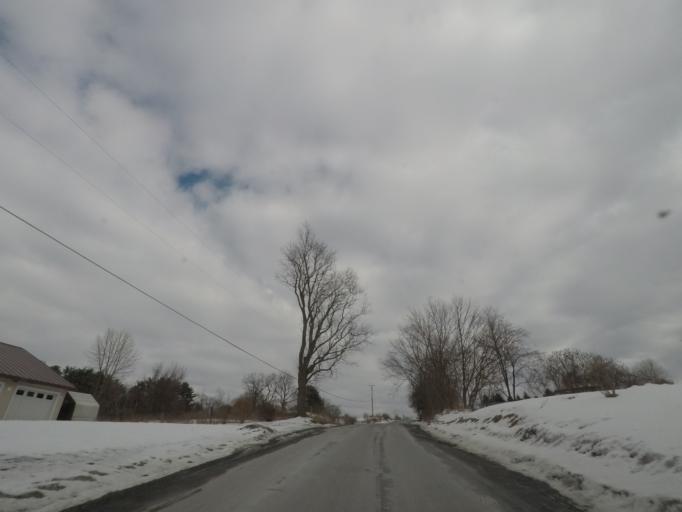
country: US
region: New York
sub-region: Rensselaer County
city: Hoosick Falls
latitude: 42.8730
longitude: -73.3976
